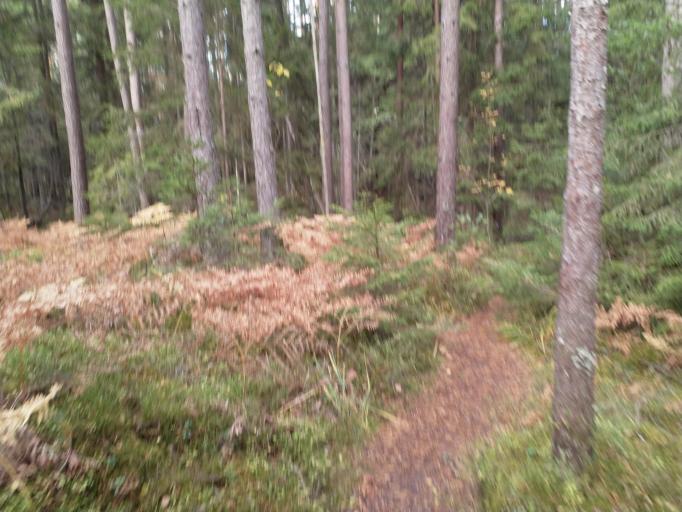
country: LV
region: Dundaga
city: Dundaga
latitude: 57.6466
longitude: 22.2592
